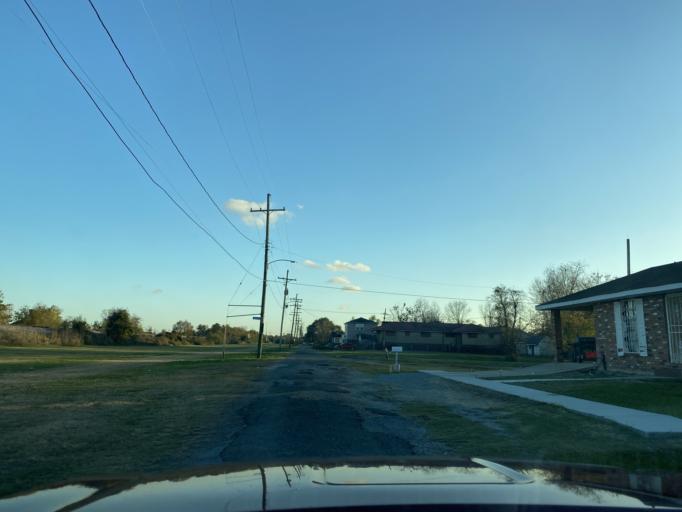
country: US
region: Louisiana
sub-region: Orleans Parish
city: New Orleans
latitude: 30.0212
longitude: -90.0473
